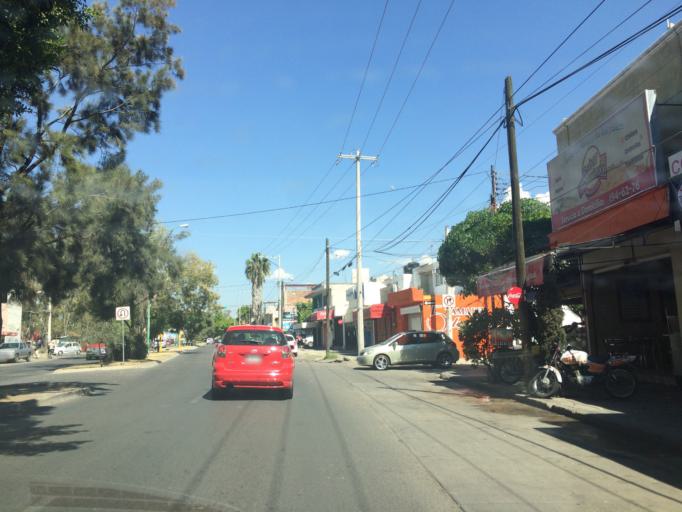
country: MX
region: Guanajuato
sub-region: Leon
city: San Jose de Duran (Los Troncoso)
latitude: 21.0916
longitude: -101.6475
